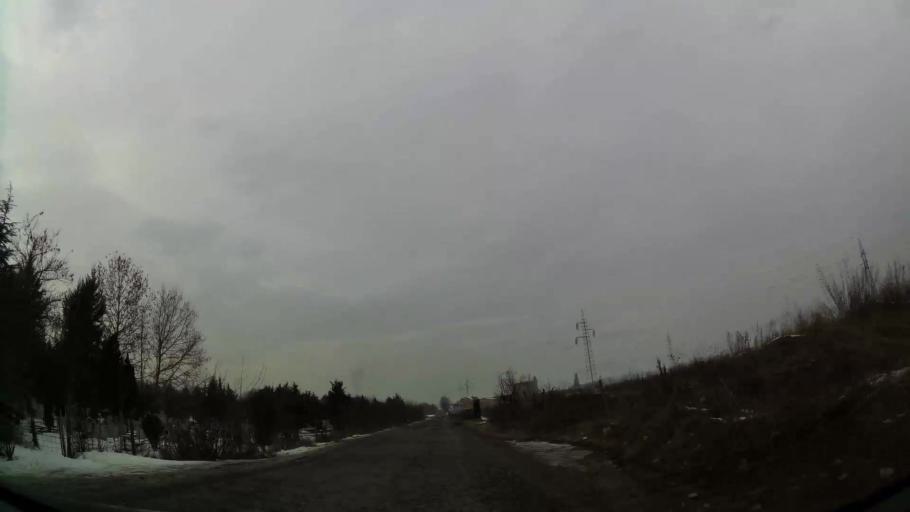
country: MK
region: Suto Orizari
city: Suto Orizare
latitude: 42.0444
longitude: 21.4345
